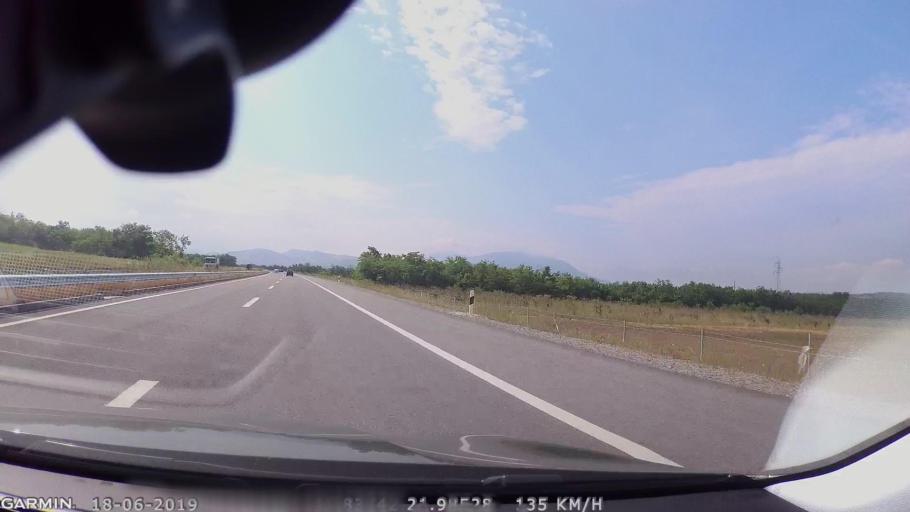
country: MK
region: Sveti Nikole
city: Sveti Nikole
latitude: 41.8459
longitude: 21.9734
